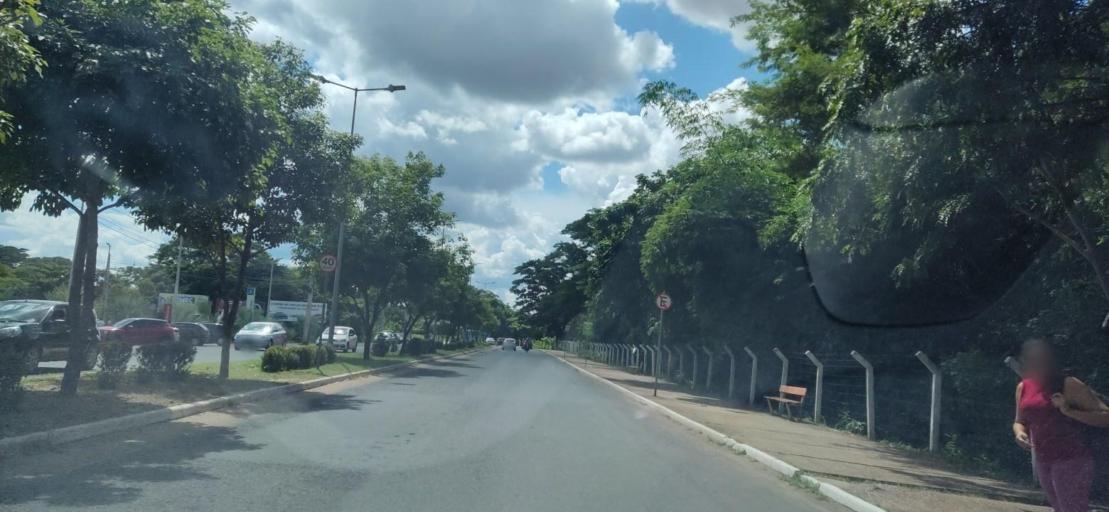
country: BR
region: Maranhao
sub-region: Timon
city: Timon
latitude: -5.0915
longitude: -42.8231
